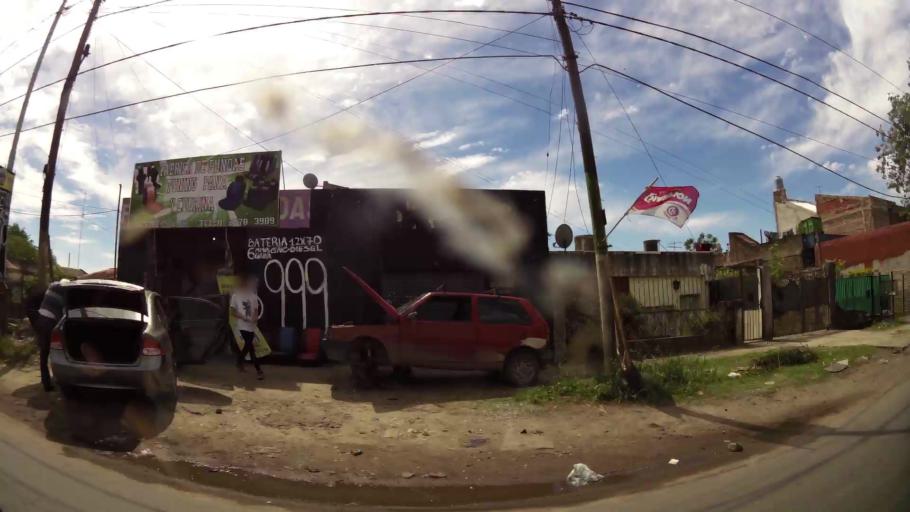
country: AR
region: Buenos Aires
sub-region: Partido de Quilmes
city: Quilmes
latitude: -34.7758
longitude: -58.2845
